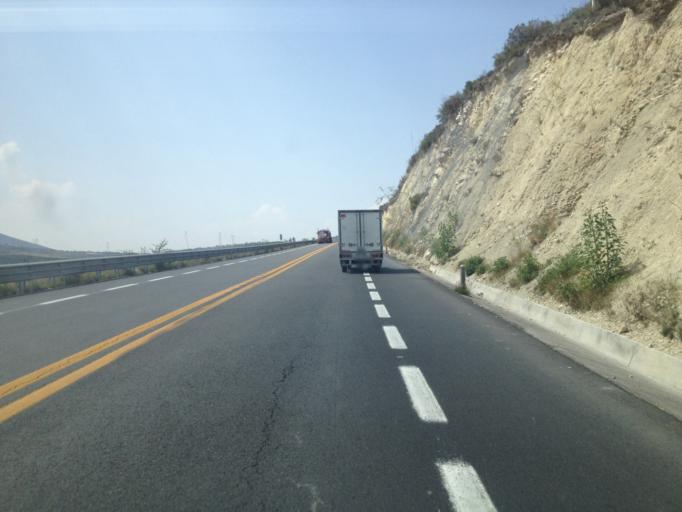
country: MX
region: Puebla
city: Morelos Canada
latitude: 18.6768
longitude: -97.4603
